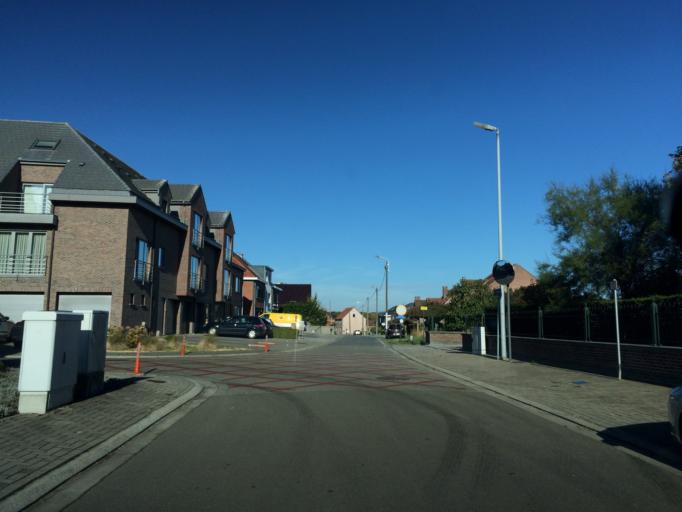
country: BE
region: Flanders
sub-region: Provincie Vlaams-Brabant
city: Merchtem
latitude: 50.9864
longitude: 4.2268
